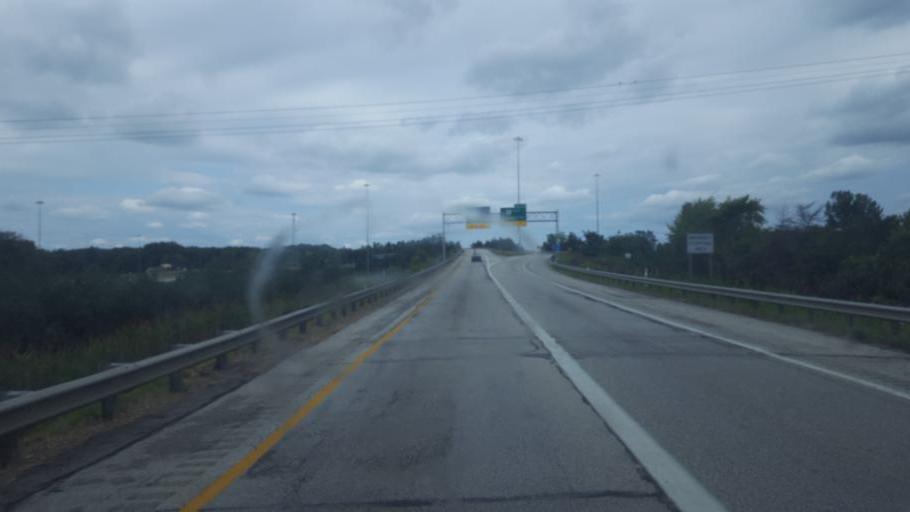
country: US
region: Ohio
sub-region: Lake County
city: Fairport Harbor
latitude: 41.7191
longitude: -81.2798
